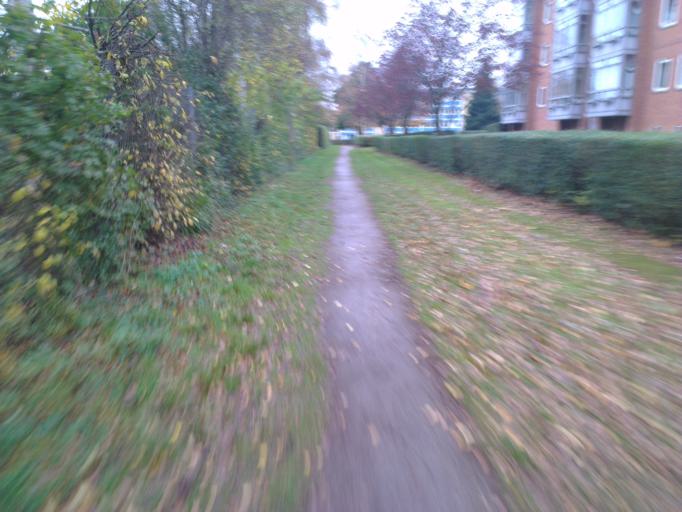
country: DK
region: Capital Region
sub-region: Frederikssund Kommune
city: Frederikssund
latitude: 55.8409
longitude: 12.0644
